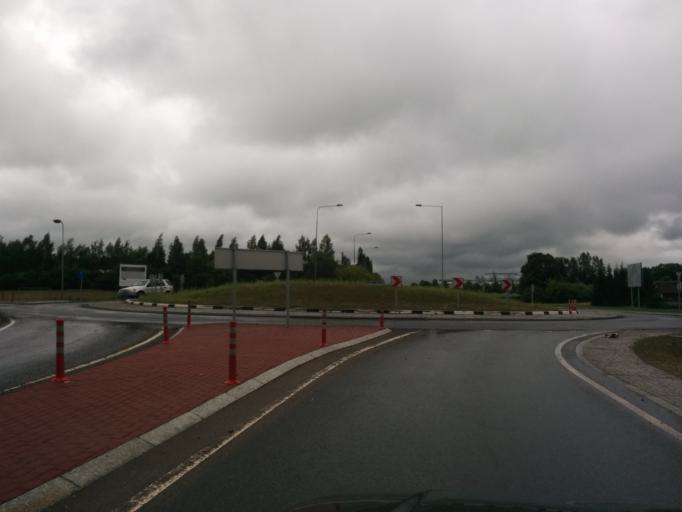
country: LT
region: Panevezys
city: Pasvalys
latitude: 56.0554
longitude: 24.4091
